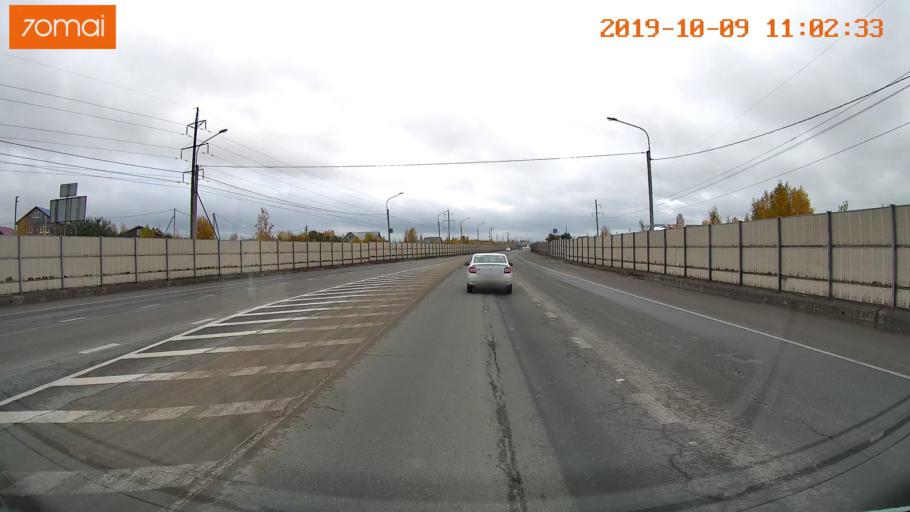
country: RU
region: Vologda
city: Vologda
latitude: 59.2307
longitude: 39.7746
